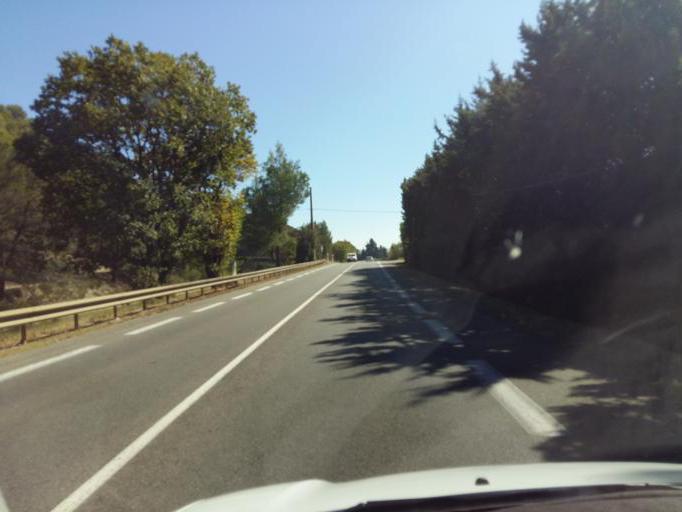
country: FR
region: Provence-Alpes-Cote d'Azur
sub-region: Departement des Bouches-du-Rhone
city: Senas
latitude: 43.7673
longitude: 5.1246
